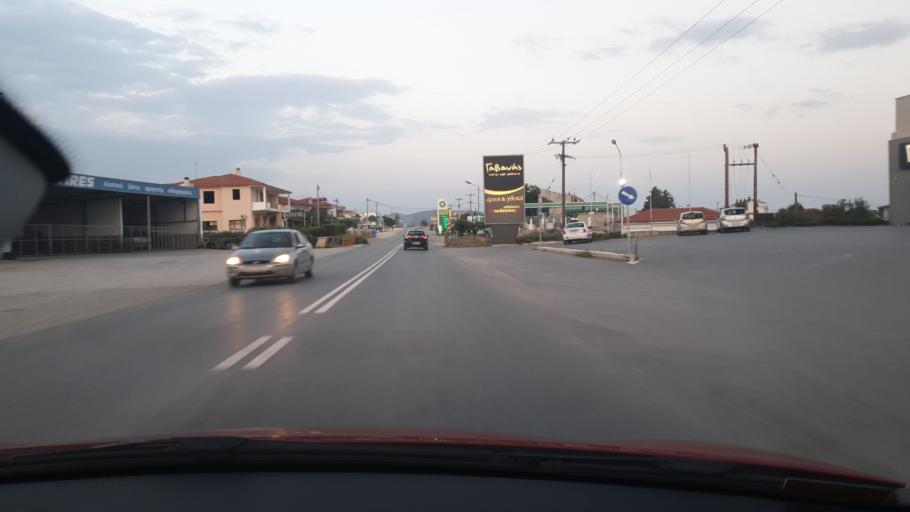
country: GR
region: Central Macedonia
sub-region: Nomos Chalkidikis
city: Kalyves Polygyrou
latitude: 40.2829
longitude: 23.3938
